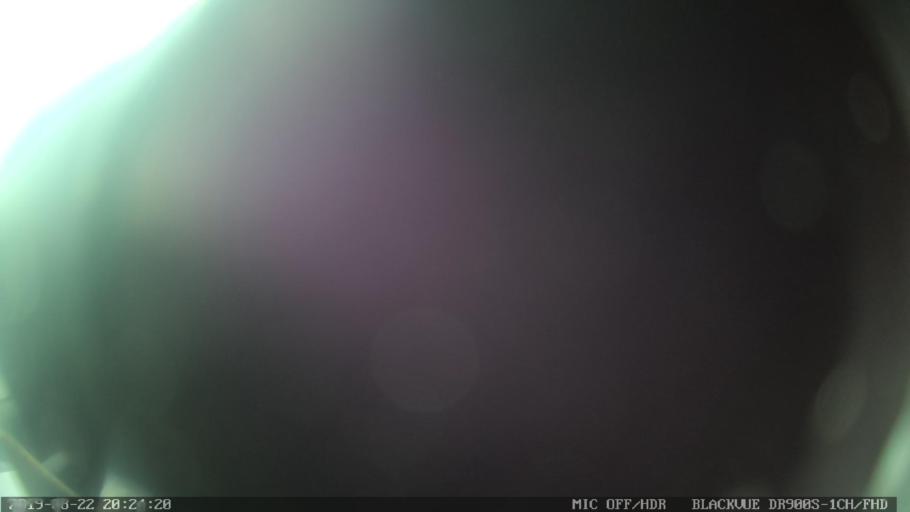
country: PT
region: Castelo Branco
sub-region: Castelo Branco
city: Castelo Branco
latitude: 39.8392
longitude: -7.5230
